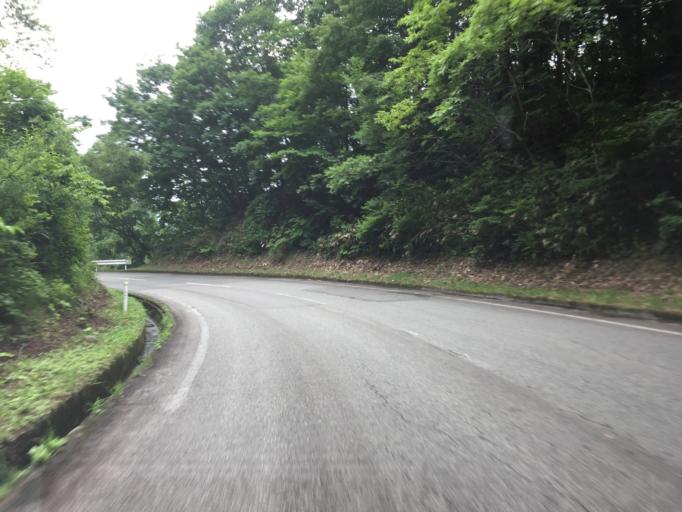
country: JP
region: Fukushima
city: Inawashiro
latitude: 37.6590
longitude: 140.1544
